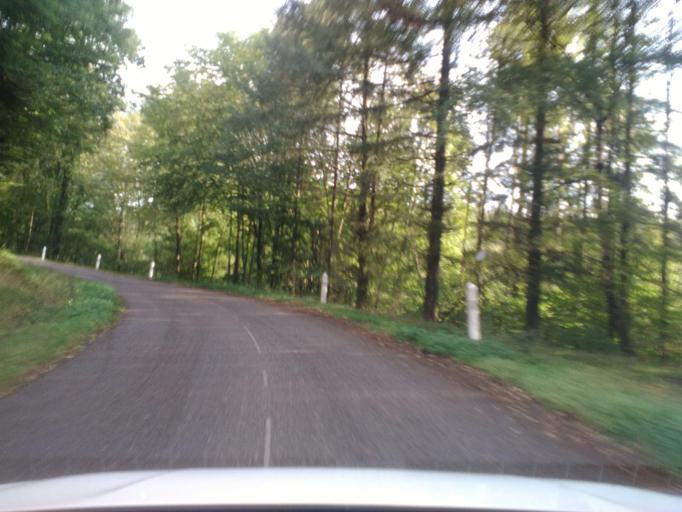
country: FR
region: Lorraine
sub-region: Departement des Vosges
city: Senones
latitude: 48.3820
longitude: 7.0434
